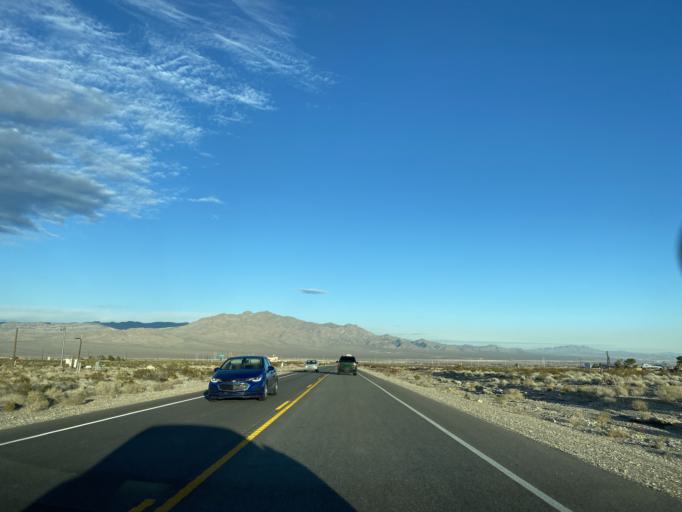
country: US
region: Nevada
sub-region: Clark County
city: Summerlin South
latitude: 36.3205
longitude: -115.3569
